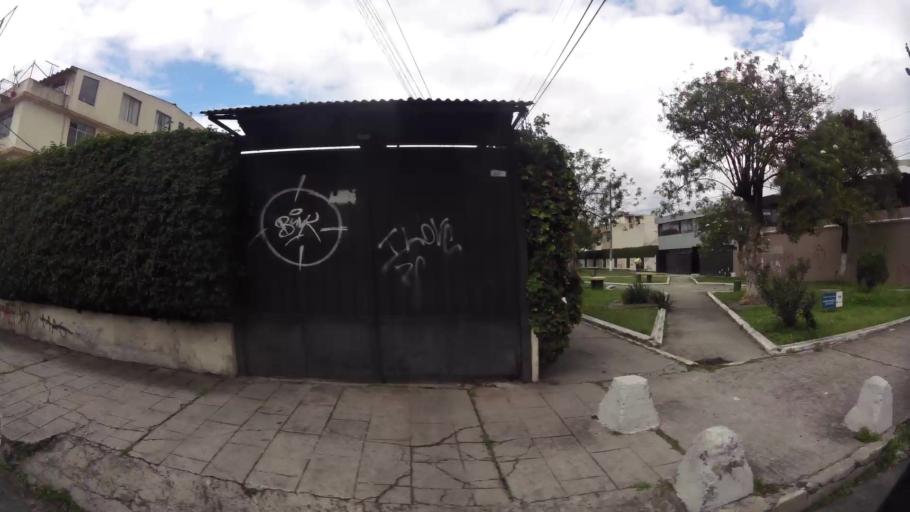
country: EC
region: Pichincha
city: Quito
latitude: -0.1614
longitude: -78.4821
